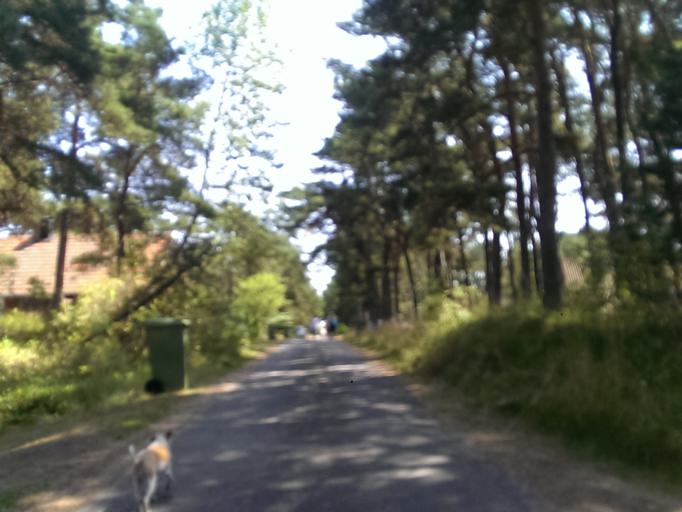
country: SE
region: Skane
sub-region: Simrishamns Kommun
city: Simrishamn
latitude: 55.4280
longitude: 14.2274
